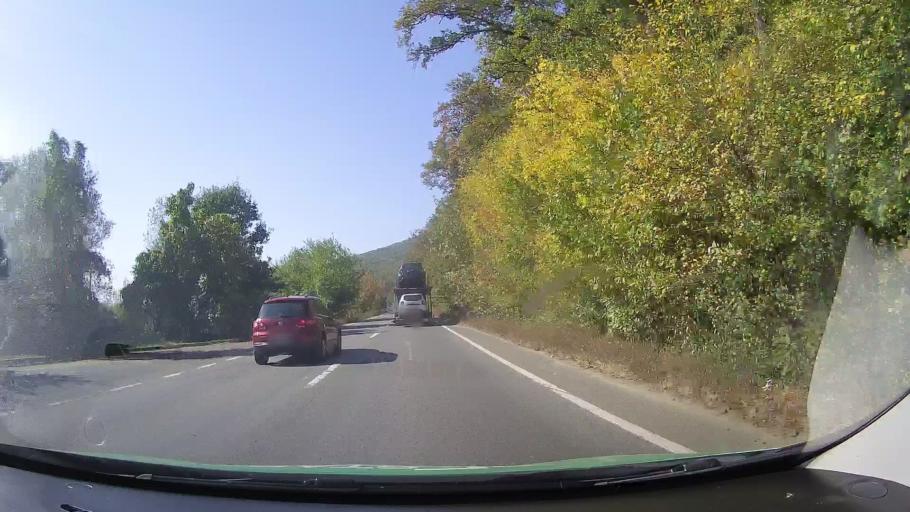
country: RO
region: Arad
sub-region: Comuna Barzava
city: Barzava
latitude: 46.1033
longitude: 21.9364
